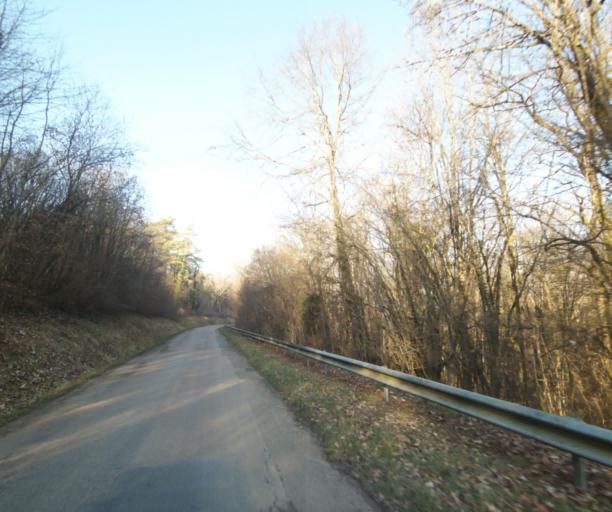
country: FR
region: Champagne-Ardenne
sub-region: Departement de la Haute-Marne
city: Chevillon
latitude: 48.5189
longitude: 5.0918
